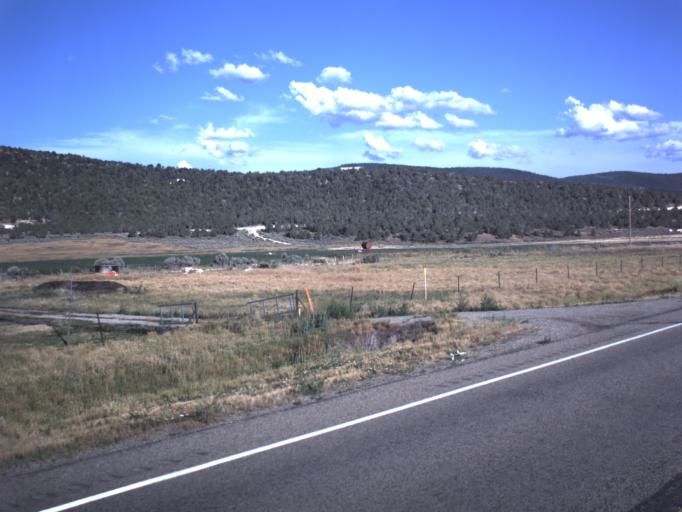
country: US
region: Utah
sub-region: Sanpete County
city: Fairview
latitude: 39.7767
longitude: -111.4902
